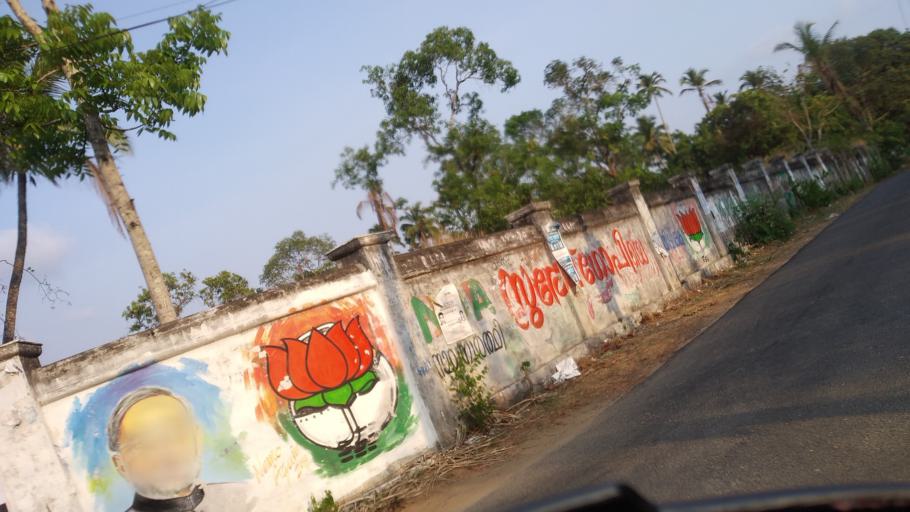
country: IN
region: Kerala
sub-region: Thrissur District
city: Thanniyam
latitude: 10.4317
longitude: 76.0792
